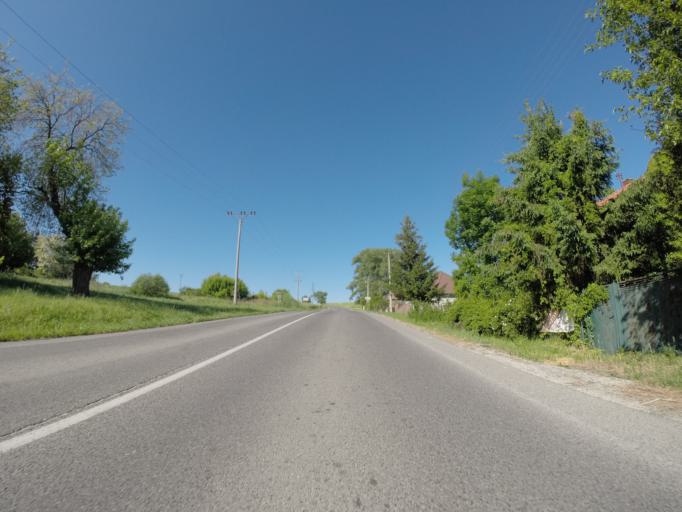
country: SK
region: Nitriansky
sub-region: Okres Nitra
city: Nitra
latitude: 48.5311
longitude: 18.0944
